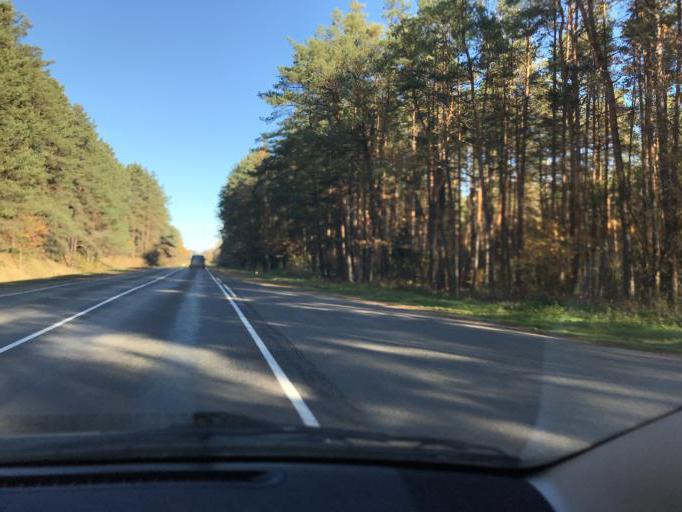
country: BY
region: Vitebsk
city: Polatsk
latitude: 55.3195
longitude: 28.7791
